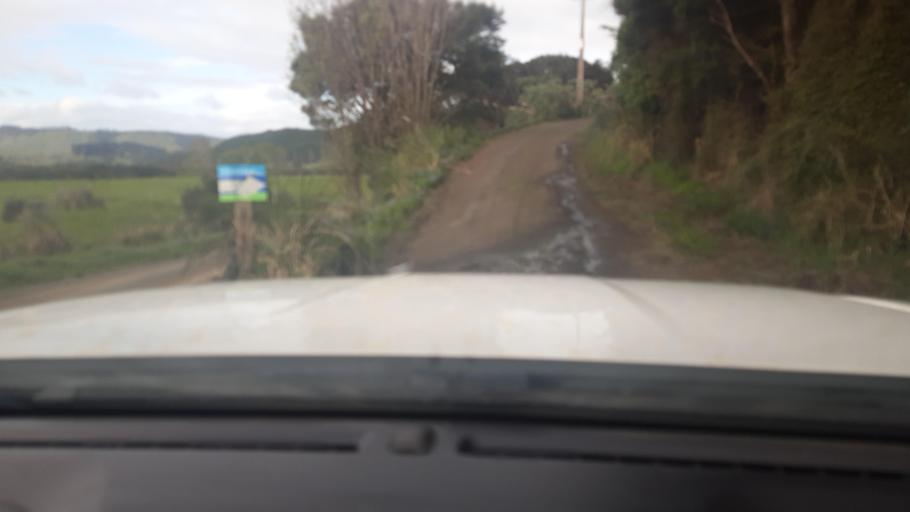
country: NZ
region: Northland
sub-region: Far North District
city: Ahipara
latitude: -35.2596
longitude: 173.2007
